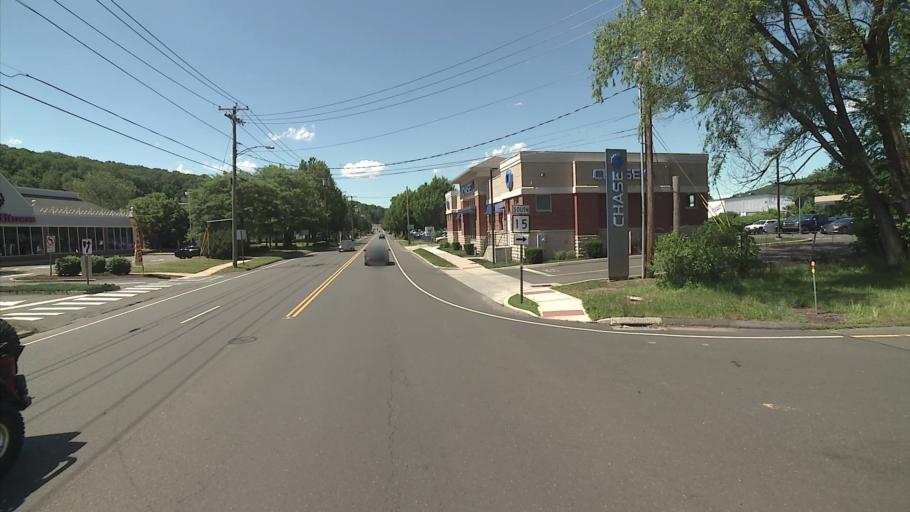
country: US
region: Connecticut
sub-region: New Haven County
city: Woodbridge
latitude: 41.3381
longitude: -72.9798
